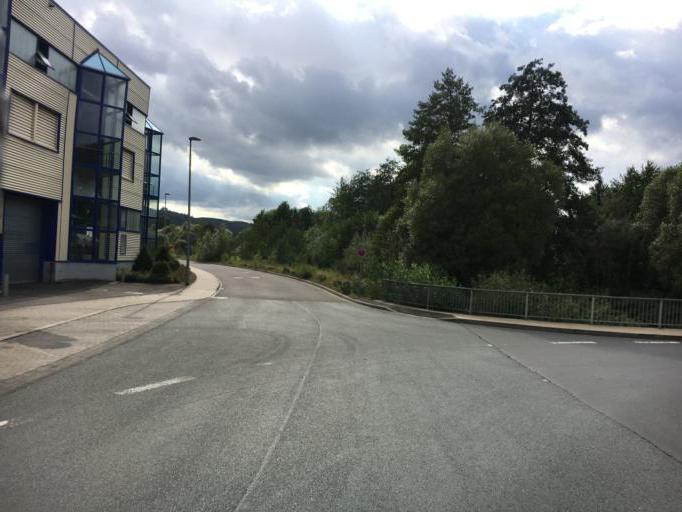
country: DE
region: North Rhine-Westphalia
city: Plettenberg
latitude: 51.1965
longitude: 7.8225
